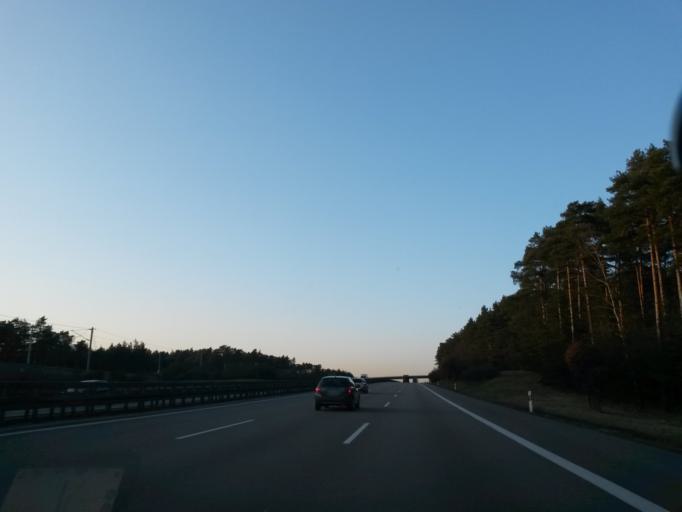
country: DE
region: Bavaria
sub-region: Regierungsbezirk Mittelfranken
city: Allersberg
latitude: 49.2749
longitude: 11.2105
